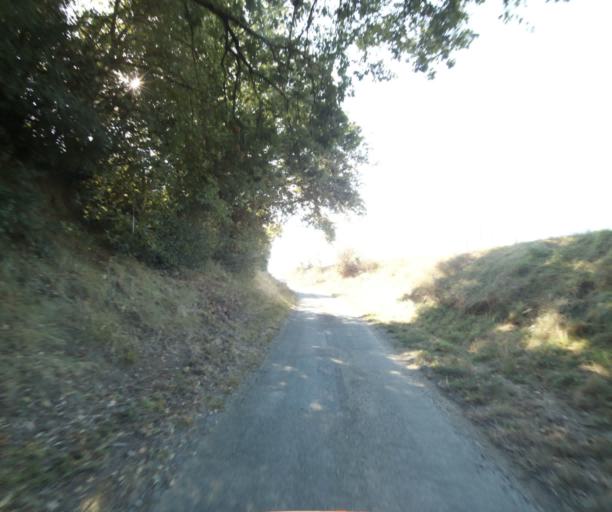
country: FR
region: Midi-Pyrenees
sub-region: Departement du Tarn-et-Garonne
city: Verdun-sur-Garonne
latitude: 43.8630
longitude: 1.2238
